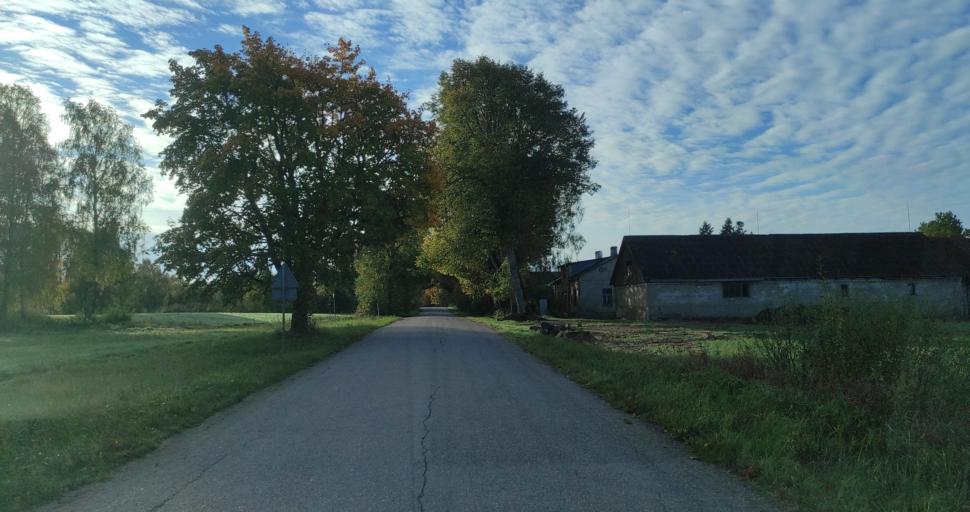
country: LV
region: Skrunda
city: Skrunda
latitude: 56.7446
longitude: 21.8783
